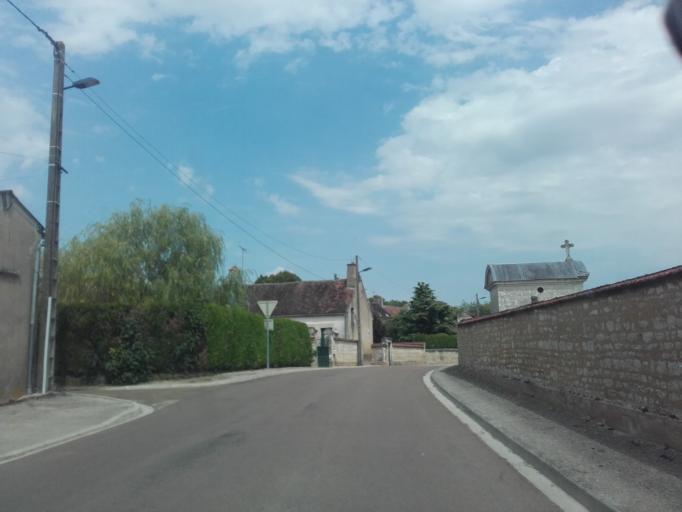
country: FR
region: Bourgogne
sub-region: Departement de l'Yonne
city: Chablis
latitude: 47.8087
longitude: 3.7992
